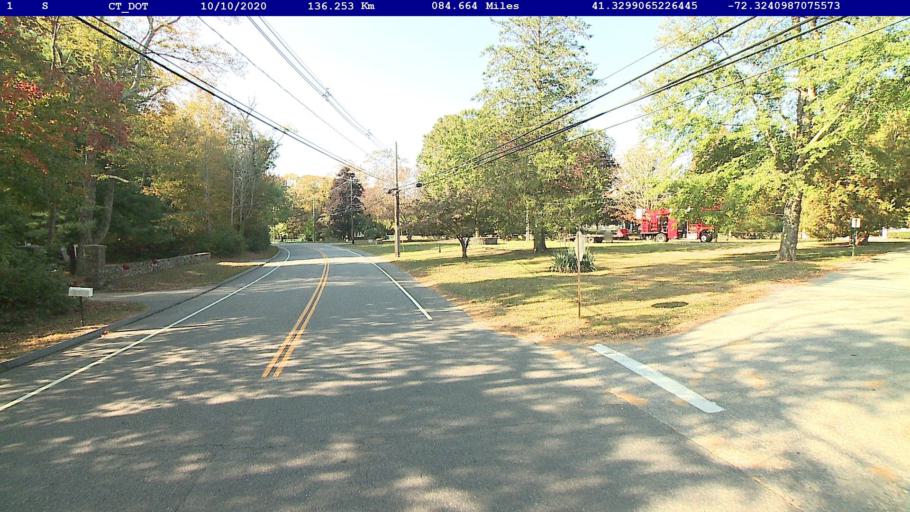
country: US
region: Connecticut
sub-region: Middlesex County
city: Old Saybrook Center
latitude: 41.3299
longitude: -72.3240
